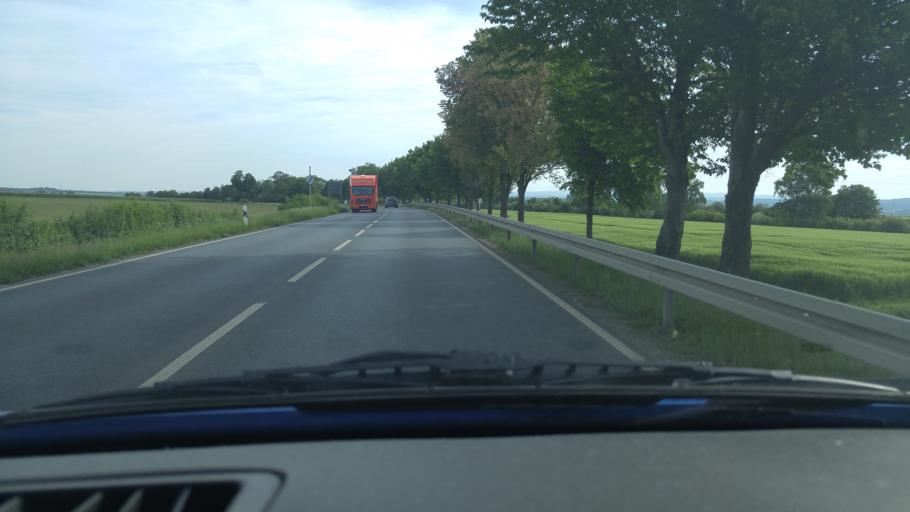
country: DE
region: Hesse
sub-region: Regierungsbezirk Darmstadt
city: Wolfersheim
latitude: 50.3857
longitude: 8.8091
